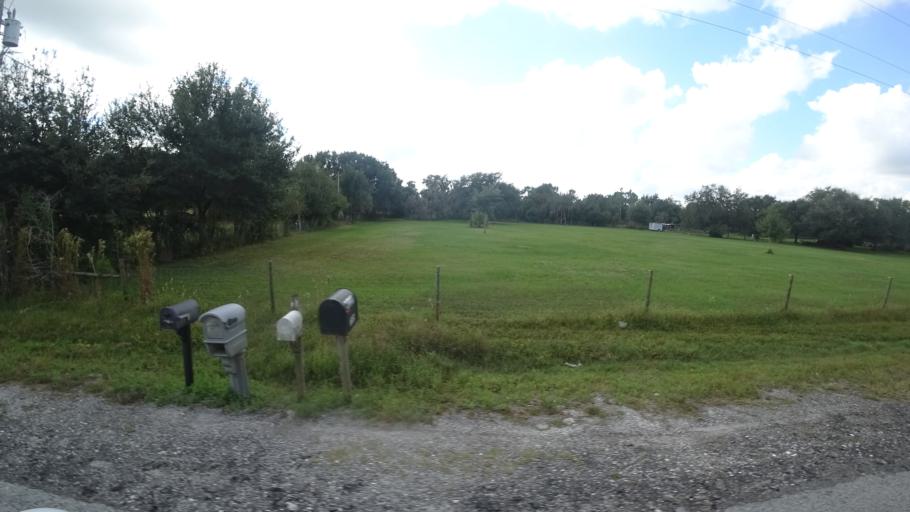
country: US
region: Florida
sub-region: Sarasota County
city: Lake Sarasota
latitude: 27.4013
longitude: -82.2689
